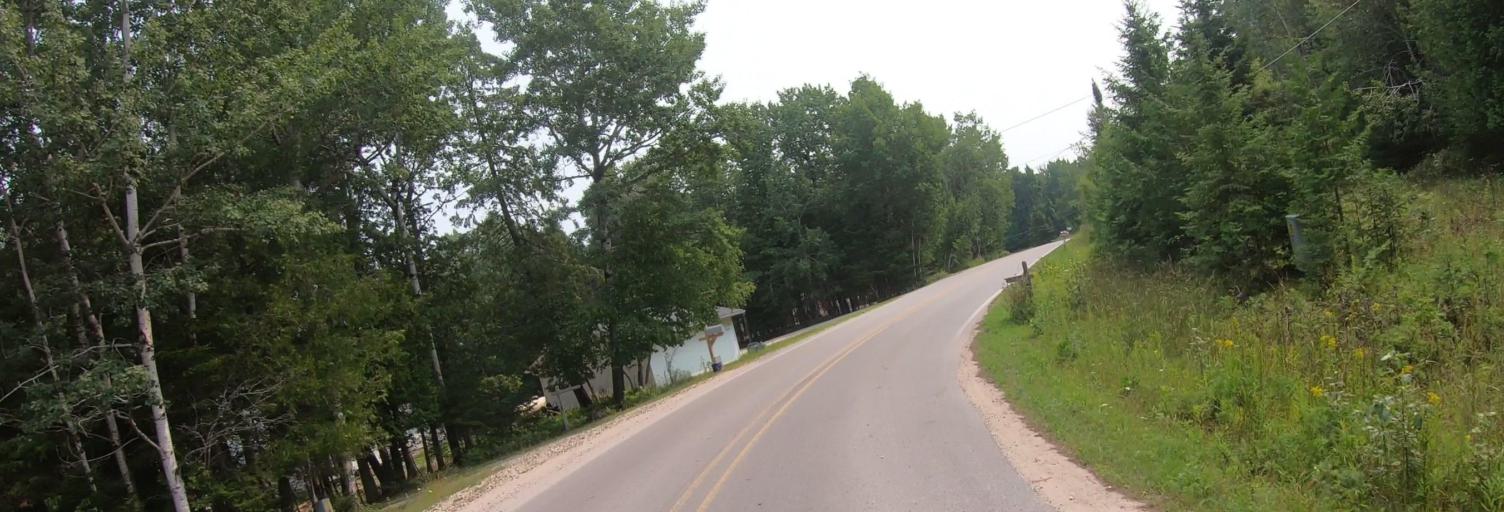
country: CA
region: Ontario
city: Thessalon
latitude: 46.0373
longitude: -83.7067
